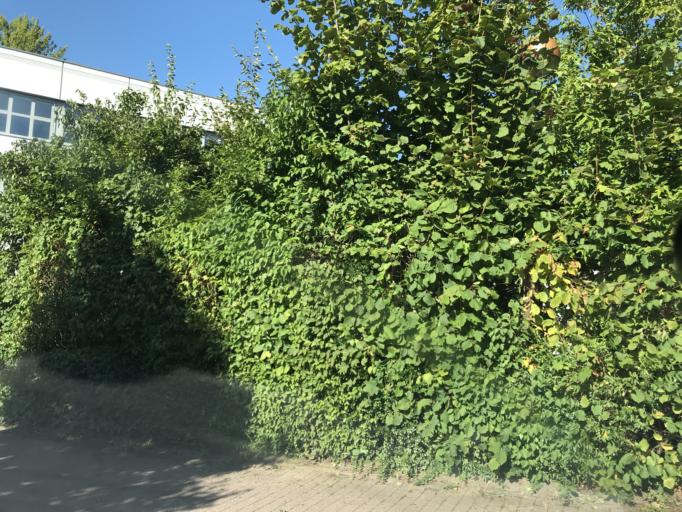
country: DE
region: Baden-Wuerttemberg
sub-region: Freiburg Region
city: Schopfheim
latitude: 47.6469
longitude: 7.8289
